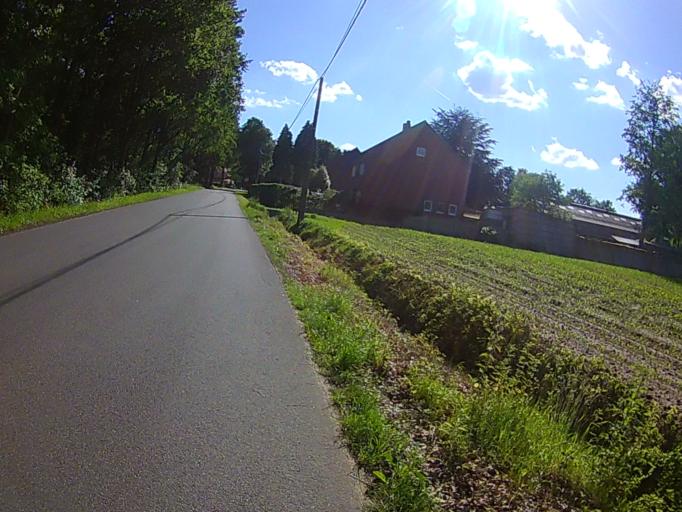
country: BE
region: Flanders
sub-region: Provincie Antwerpen
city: Herentals
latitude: 51.2073
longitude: 4.8491
